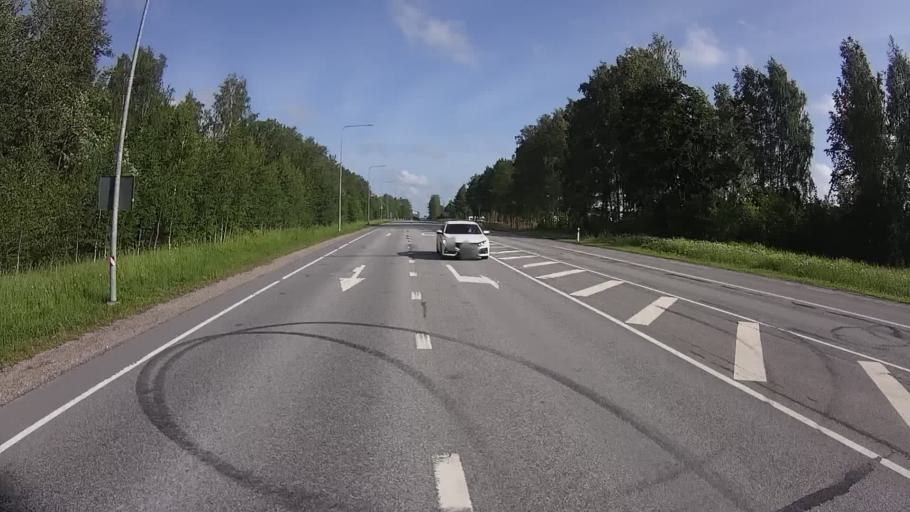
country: EE
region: Viljandimaa
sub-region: Viljandi linn
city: Viljandi
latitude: 58.3398
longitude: 25.5686
